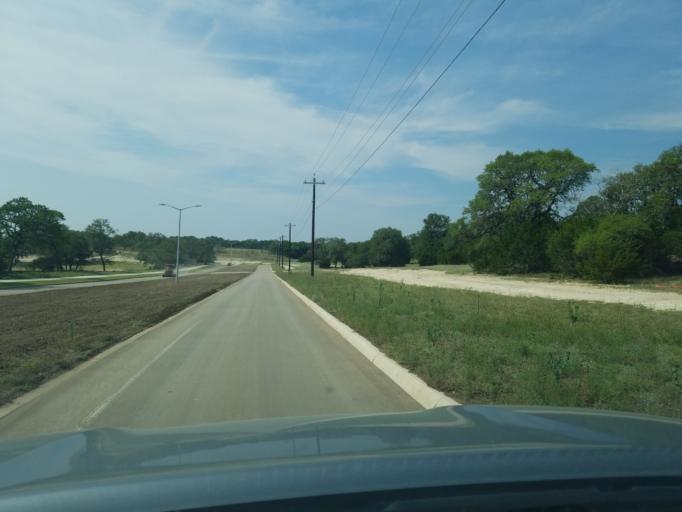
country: US
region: Texas
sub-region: Kendall County
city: Boerne
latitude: 29.7550
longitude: -98.7191
